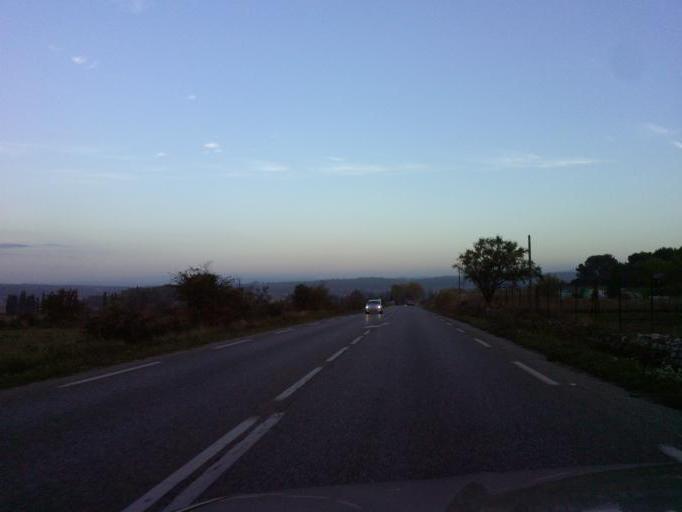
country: FR
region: Provence-Alpes-Cote d'Azur
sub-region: Departement des Bouches-du-Rhone
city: Saint-Cannat
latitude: 43.6266
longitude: 5.2915
